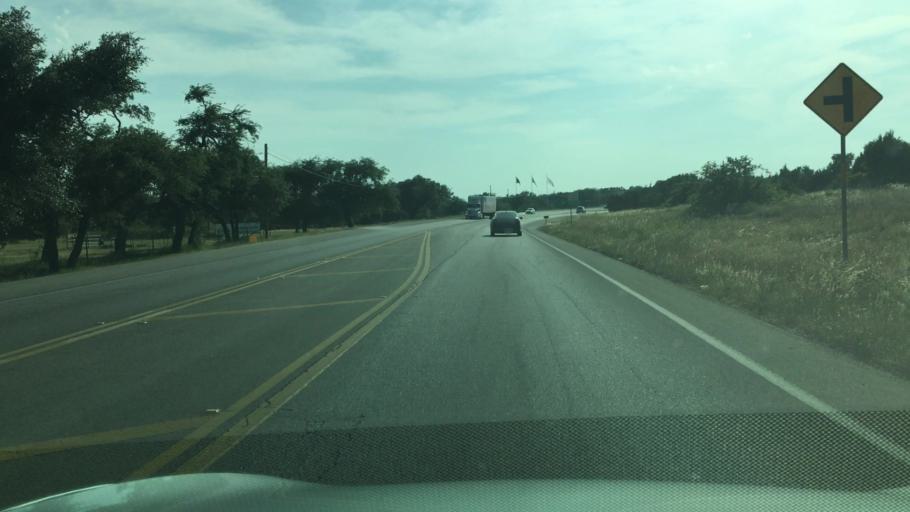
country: US
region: Texas
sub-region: Hays County
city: Wimberley
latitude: 29.9169
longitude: -98.0460
